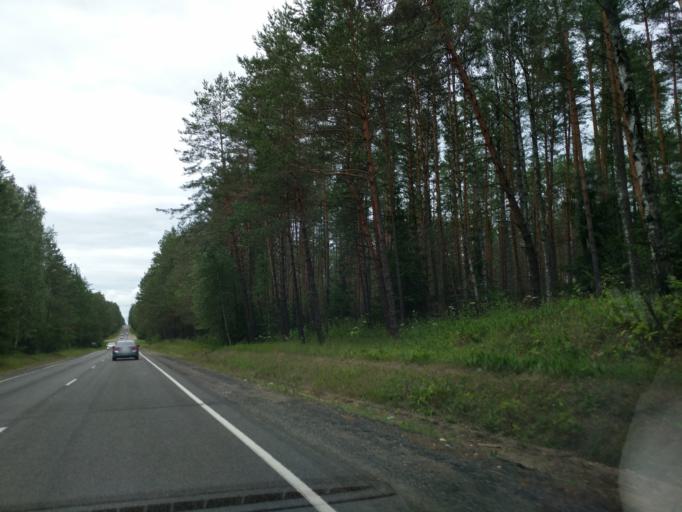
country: BY
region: Minsk
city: Myadzyel
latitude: 54.8017
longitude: 27.0002
